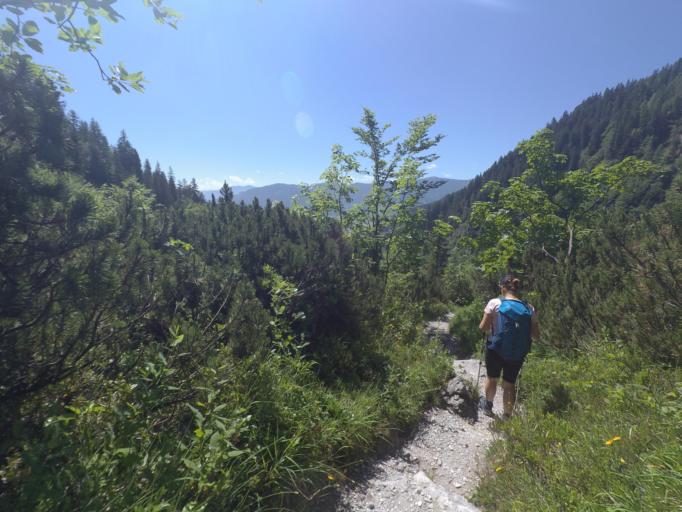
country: AT
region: Salzburg
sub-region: Politischer Bezirk Zell am See
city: Leogang
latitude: 47.4637
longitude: 12.7465
